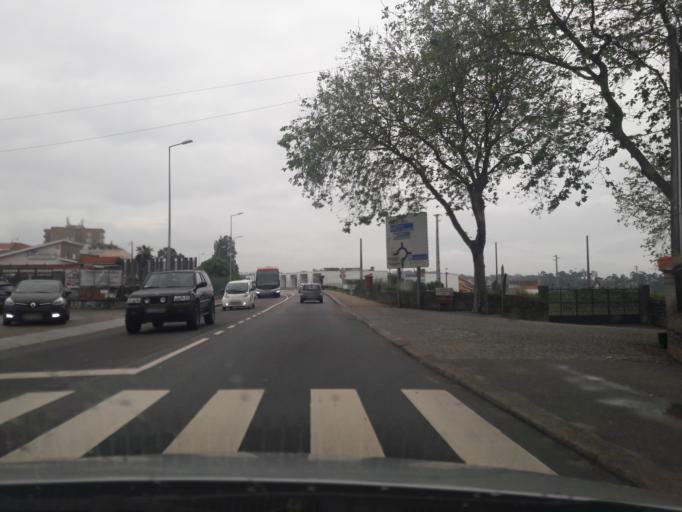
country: PT
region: Porto
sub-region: Vila do Conde
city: Vila do Conde
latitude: 41.3437
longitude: -8.7362
